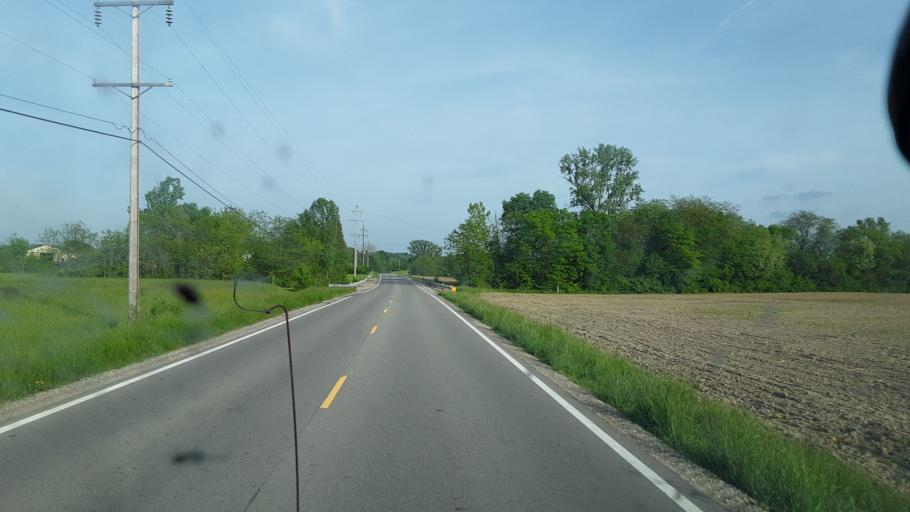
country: US
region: Ohio
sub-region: Ross County
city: Kingston
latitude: 39.5439
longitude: -82.8509
